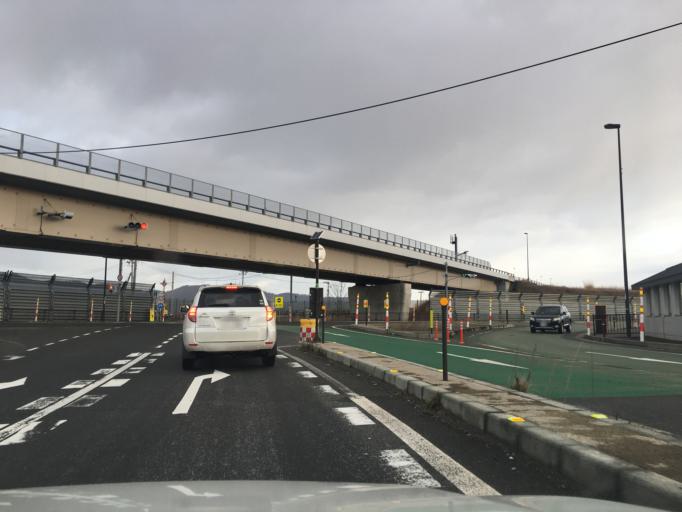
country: JP
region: Yamagata
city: Tsuruoka
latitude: 38.7170
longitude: 139.7592
